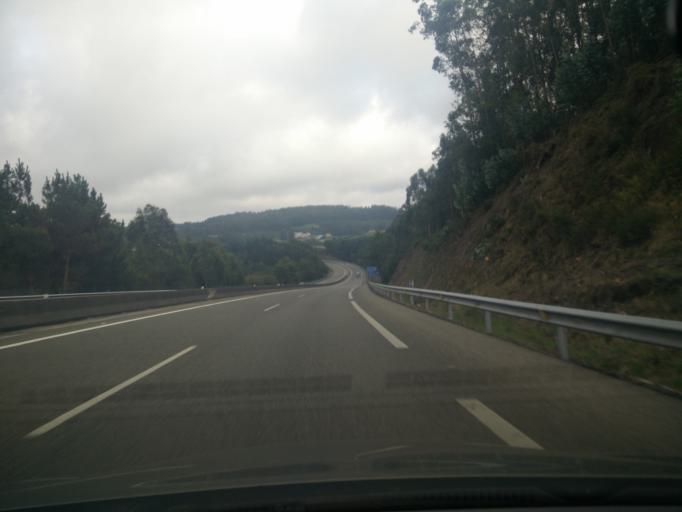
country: ES
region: Galicia
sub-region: Provincia da Coruna
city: Laracha
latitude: 43.2680
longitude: -8.5565
